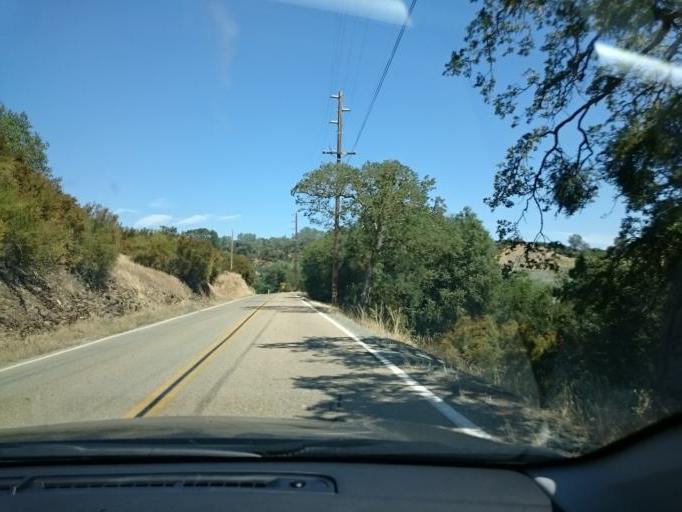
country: US
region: California
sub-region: Calaveras County
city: Rancho Calaveras
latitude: 38.1488
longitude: -120.8290
